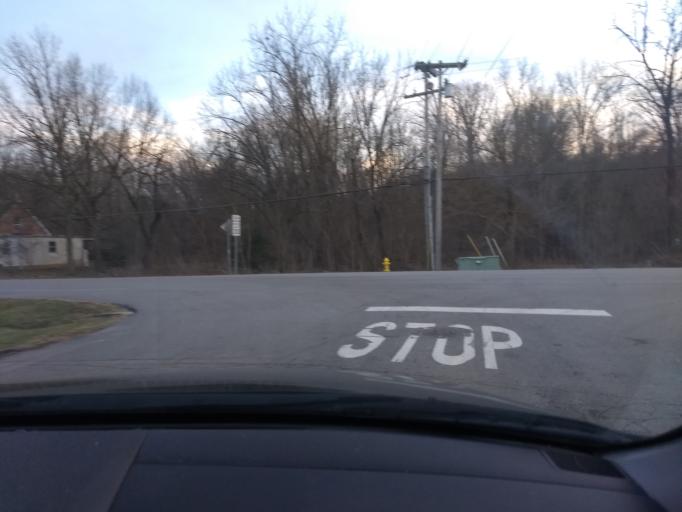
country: US
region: Indiana
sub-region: Floyd County
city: Georgetown
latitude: 38.2959
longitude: -85.9835
